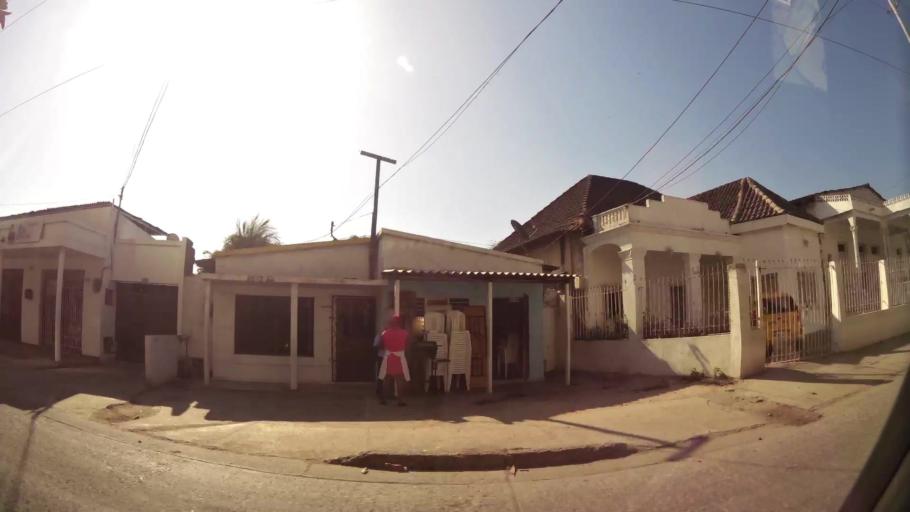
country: CO
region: Bolivar
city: Cartagena
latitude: 10.4328
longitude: -75.5343
